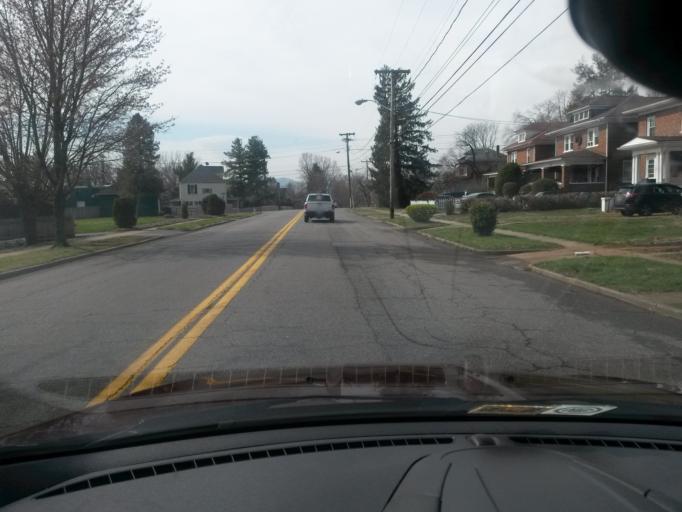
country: US
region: Virginia
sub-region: City of Roanoke
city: Roanoke
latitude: 37.2958
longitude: -79.9732
